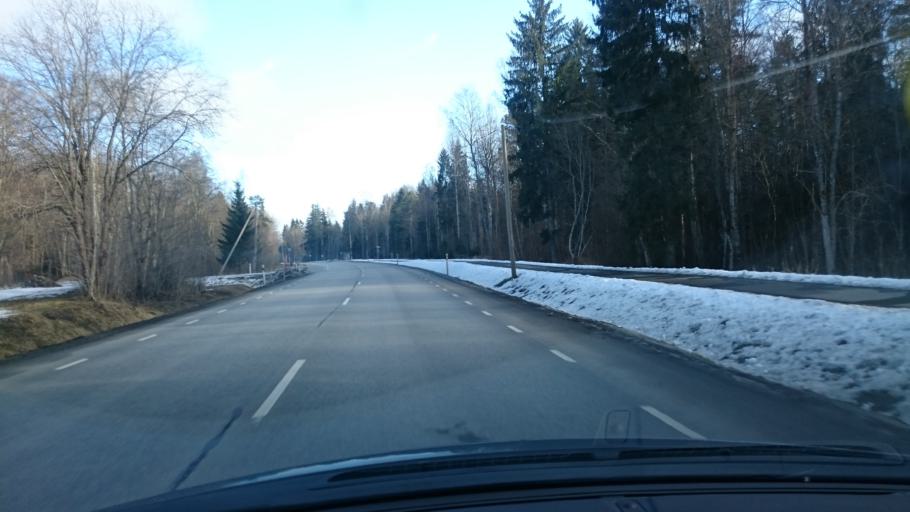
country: EE
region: Harju
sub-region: Kiili vald
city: Kiili
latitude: 59.3487
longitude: 24.7978
